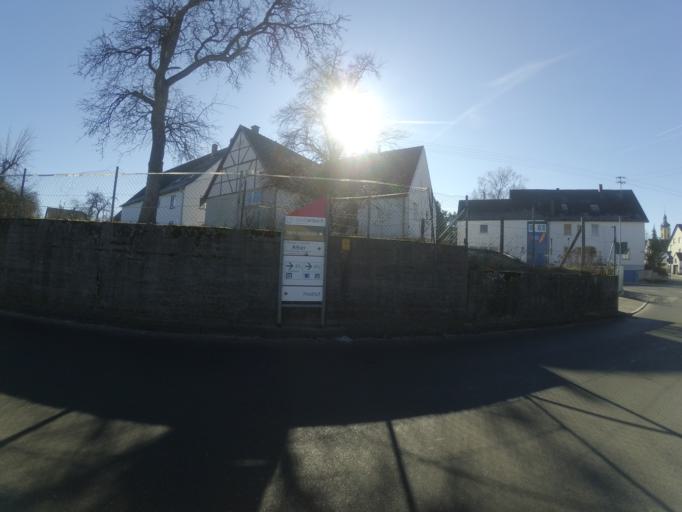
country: DE
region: Baden-Wuerttemberg
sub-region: Tuebingen Region
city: Erbach
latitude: 48.3041
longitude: 9.9026
